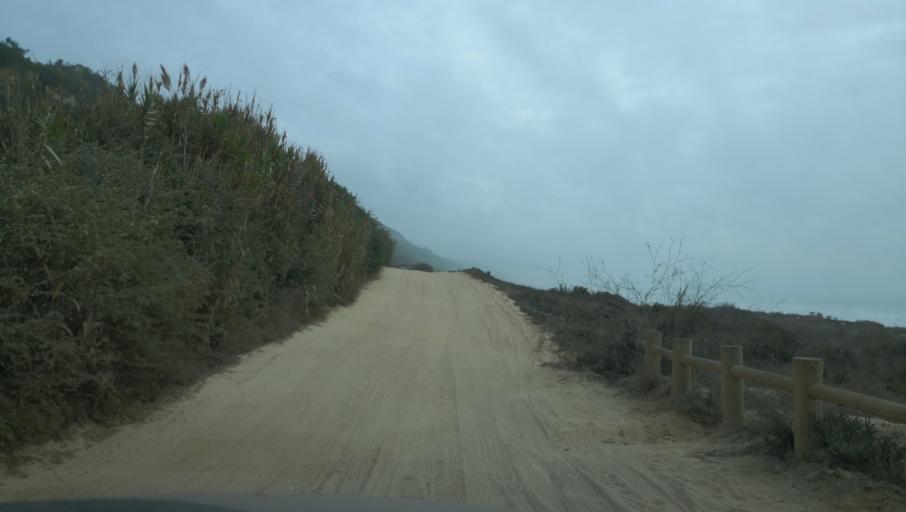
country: PT
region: Setubal
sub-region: Almada
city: Charneca
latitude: 38.5630
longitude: -9.1914
